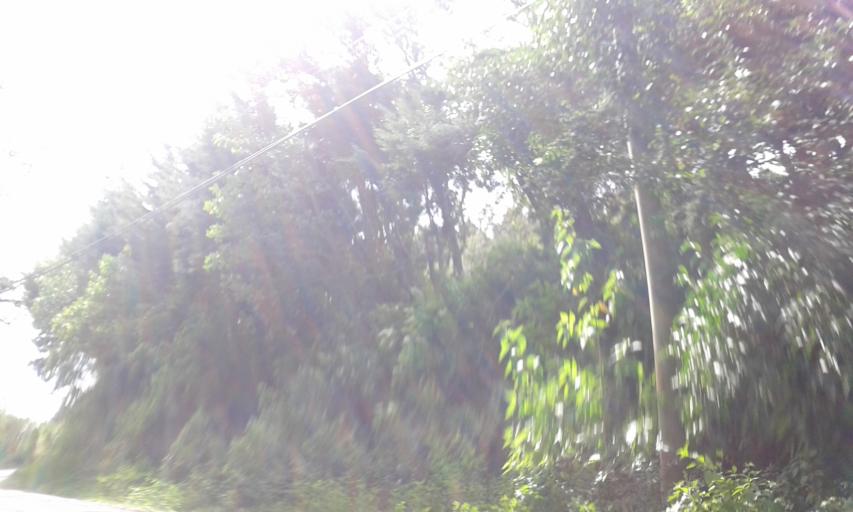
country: CR
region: Heredia
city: Santo Domingo
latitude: 10.0930
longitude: -84.1101
